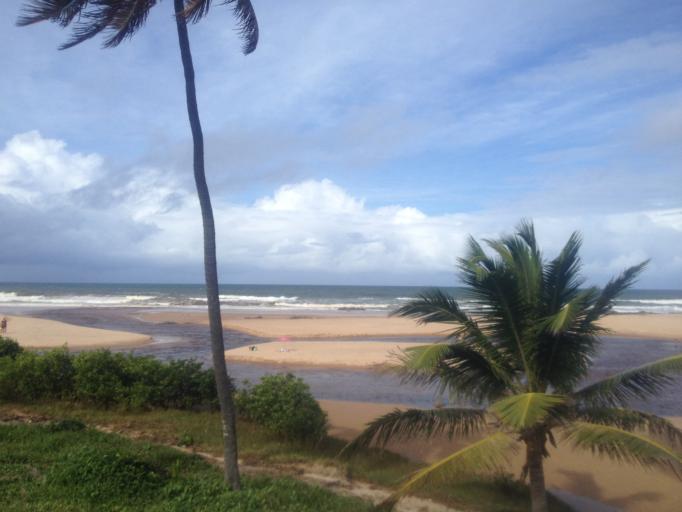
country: BR
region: Bahia
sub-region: Mata De Sao Joao
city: Mata de Sao Joao
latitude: -12.5014
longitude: -37.9616
